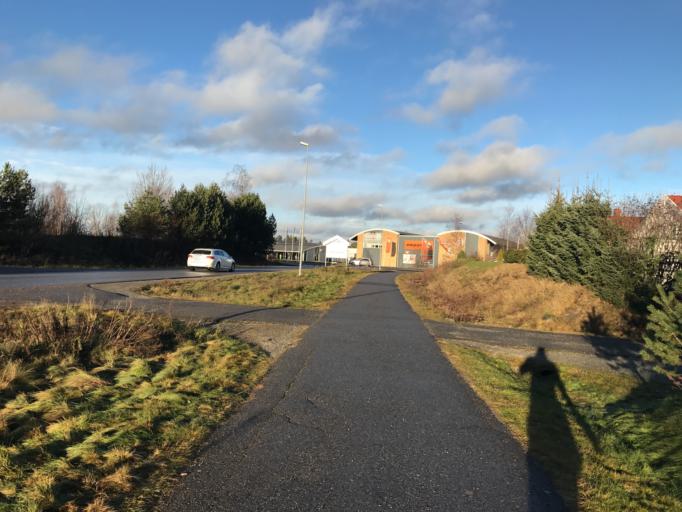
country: NO
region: Akershus
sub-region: Ullensaker
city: Jessheim
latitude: 60.1396
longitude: 11.1908
